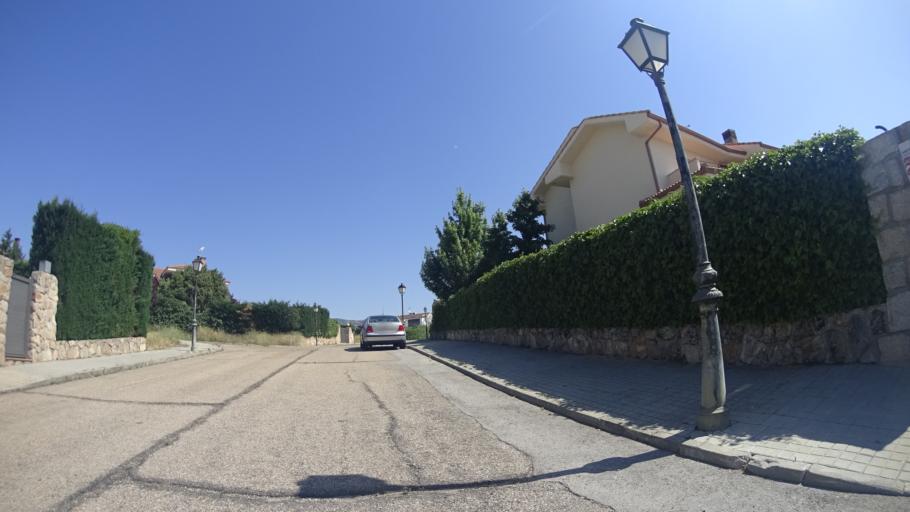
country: ES
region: Madrid
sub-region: Provincia de Madrid
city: Hoyo de Manzanares
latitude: 40.6038
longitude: -3.8986
